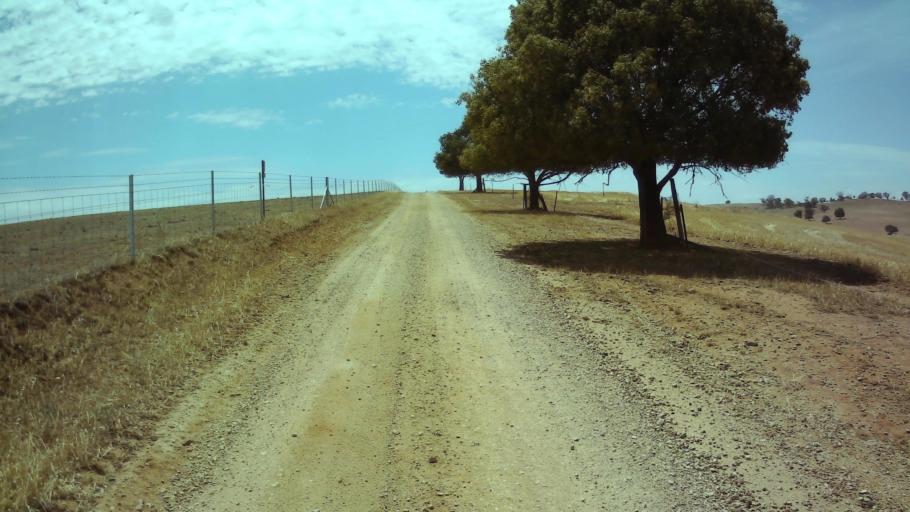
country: AU
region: New South Wales
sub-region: Cowra
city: Cowra
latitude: -33.9581
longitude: 148.4544
